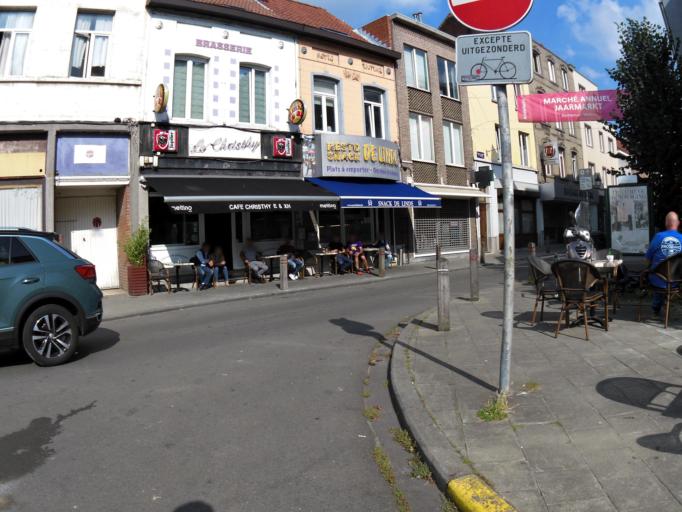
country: BE
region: Flanders
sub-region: Provincie Vlaams-Brabant
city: Dilbeek
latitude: 50.8358
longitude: 4.2999
